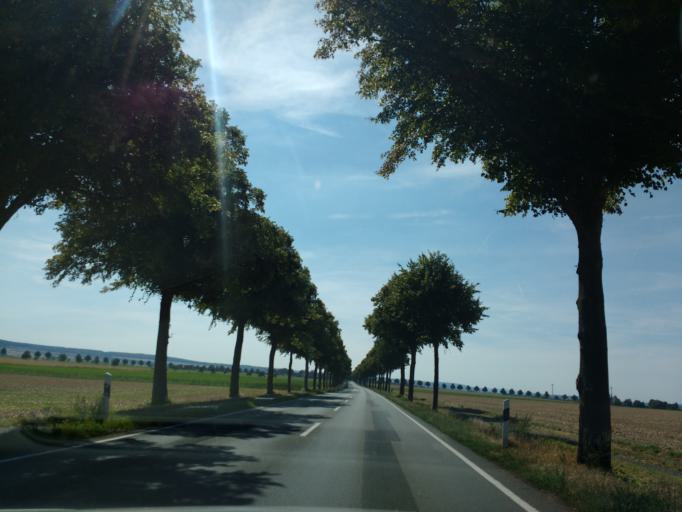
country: DE
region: Lower Saxony
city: Schellerten
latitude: 52.1777
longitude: 10.0583
